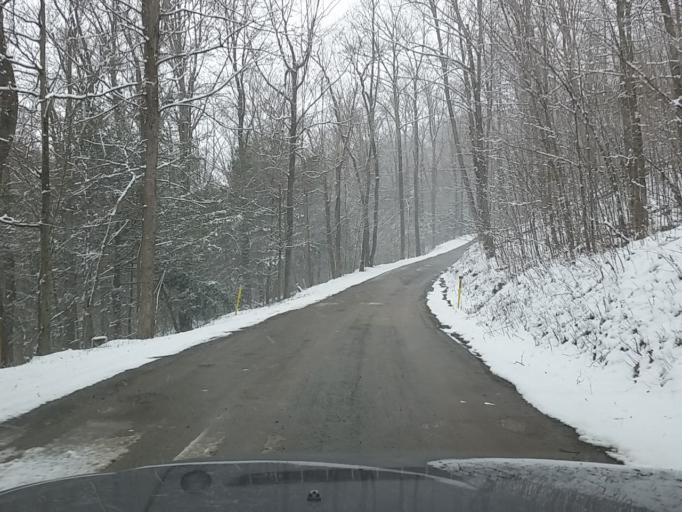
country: US
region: Pennsylvania
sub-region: Sullivan County
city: Laporte
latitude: 41.3251
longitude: -76.4588
